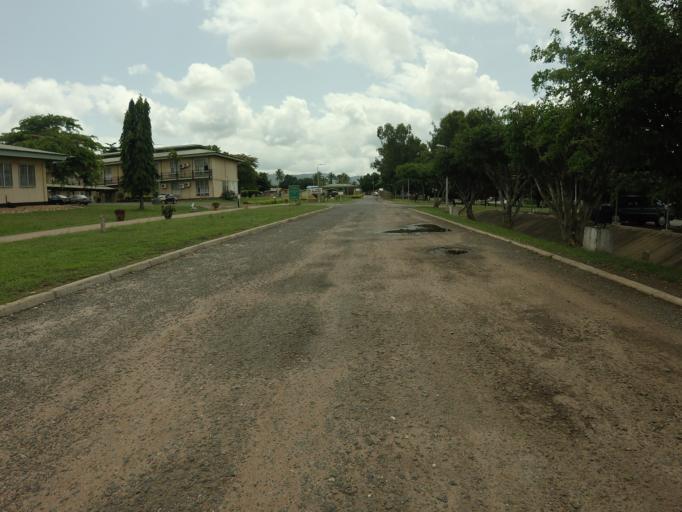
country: GH
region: Volta
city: Ho
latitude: 6.6017
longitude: 0.4847
